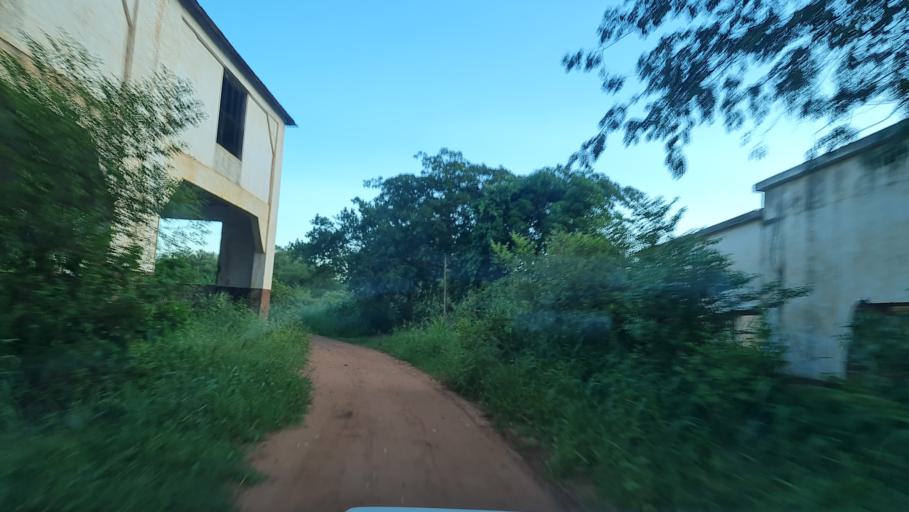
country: MZ
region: Nampula
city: Ilha de Mocambique
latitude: -14.9858
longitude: 40.0949
